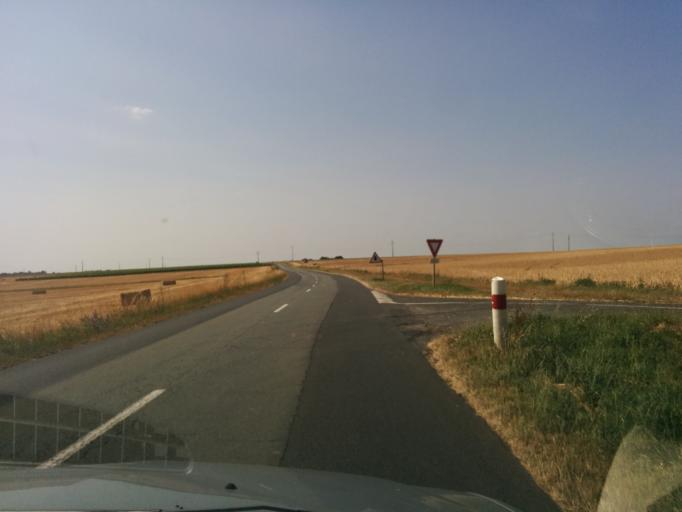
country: FR
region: Poitou-Charentes
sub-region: Departement de la Vienne
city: Mirebeau
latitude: 46.7678
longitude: 0.1493
